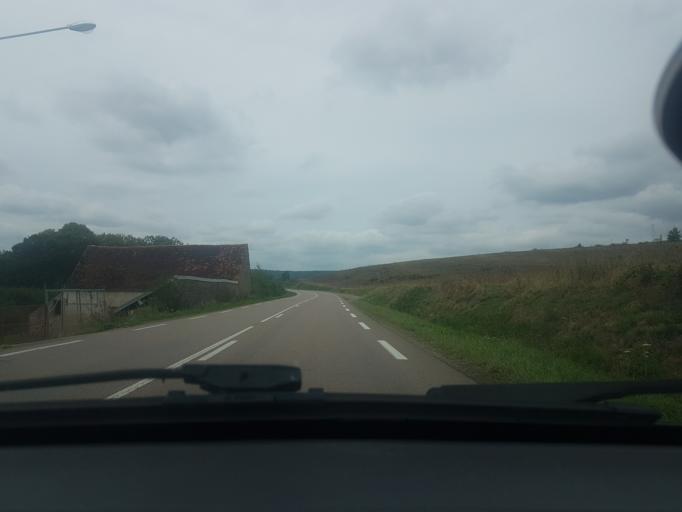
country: FR
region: Bourgogne
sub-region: Departement de la Cote-d'Or
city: Arnay-le-Duc
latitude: 47.1368
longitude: 4.4763
